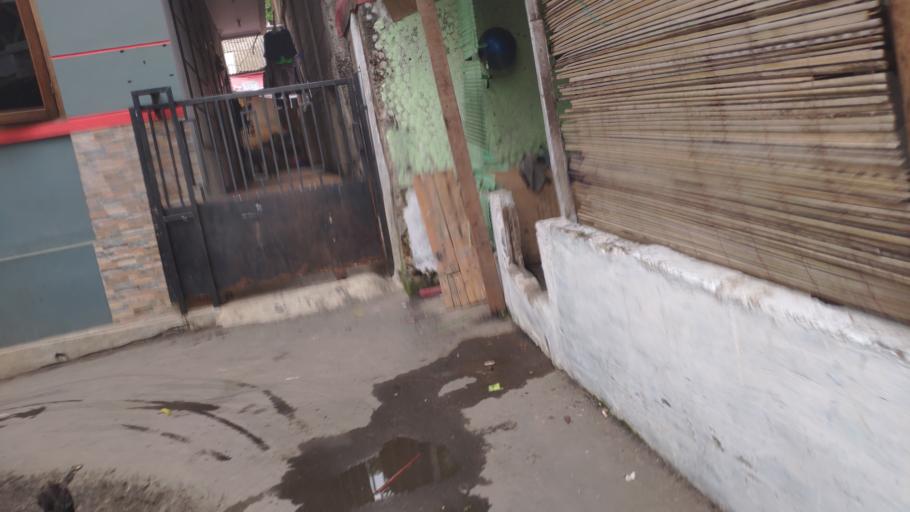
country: ID
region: Jakarta Raya
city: Jakarta
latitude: -6.2710
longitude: 106.8285
